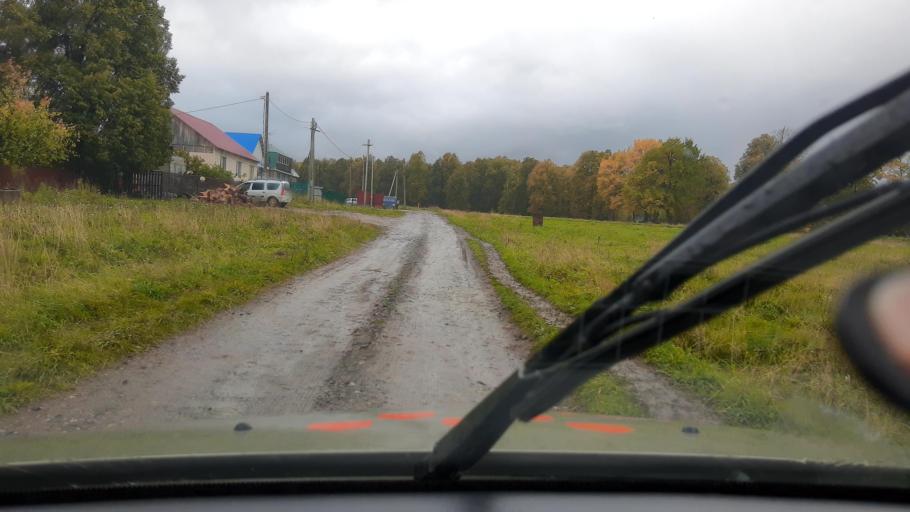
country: RU
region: Bashkortostan
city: Kudeyevskiy
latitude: 54.8754
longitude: 56.6279
